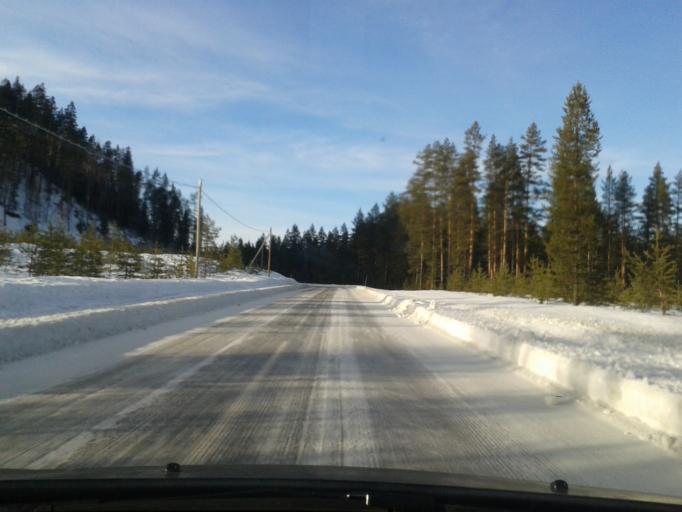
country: SE
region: Vaesternorrland
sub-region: OErnskoeldsviks Kommun
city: Bredbyn
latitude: 63.6725
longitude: 17.8221
